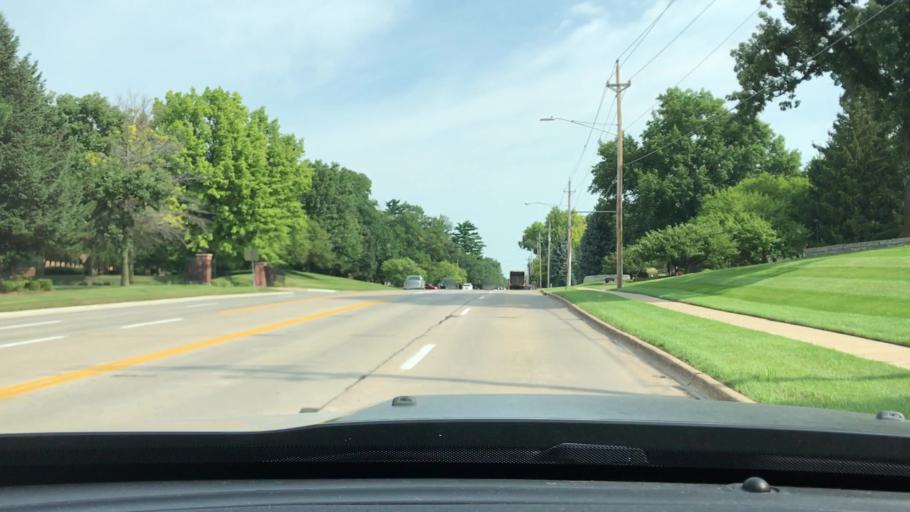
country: US
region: Iowa
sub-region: Scott County
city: Bettendorf
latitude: 41.5573
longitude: -90.5417
